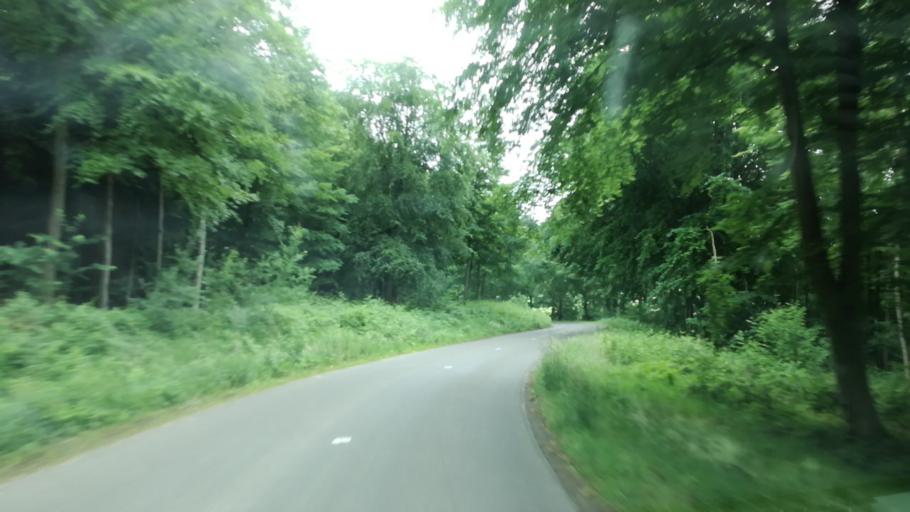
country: FR
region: Haute-Normandie
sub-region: Departement de l'Eure
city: Bourg-Achard
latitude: 49.2868
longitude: 0.8085
